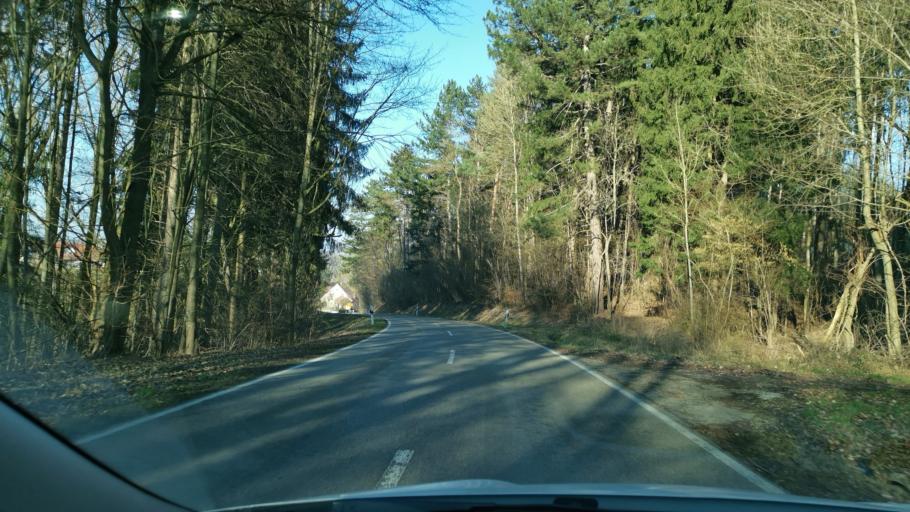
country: DE
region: Bavaria
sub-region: Swabia
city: Aindling
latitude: 48.5049
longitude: 10.9529
